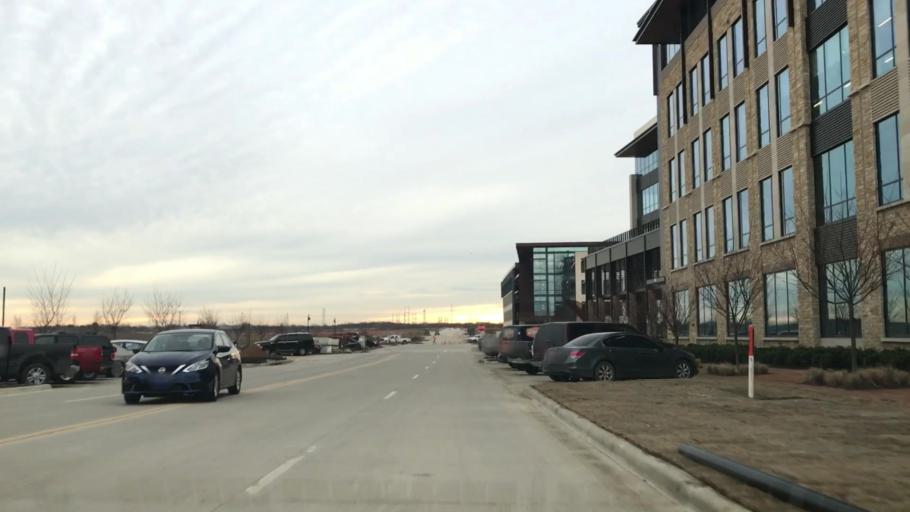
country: US
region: Texas
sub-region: Dallas County
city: Coppell
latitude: 32.9360
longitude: -96.9842
